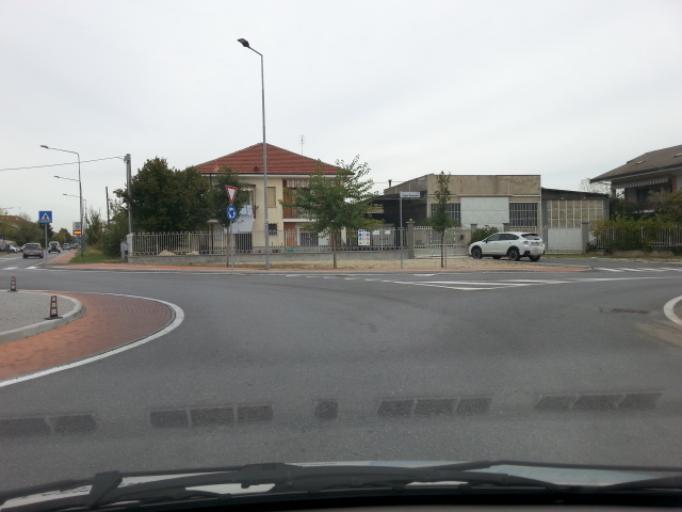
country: IT
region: Piedmont
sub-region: Provincia di Torino
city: Piossasco
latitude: 44.9809
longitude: 7.4547
